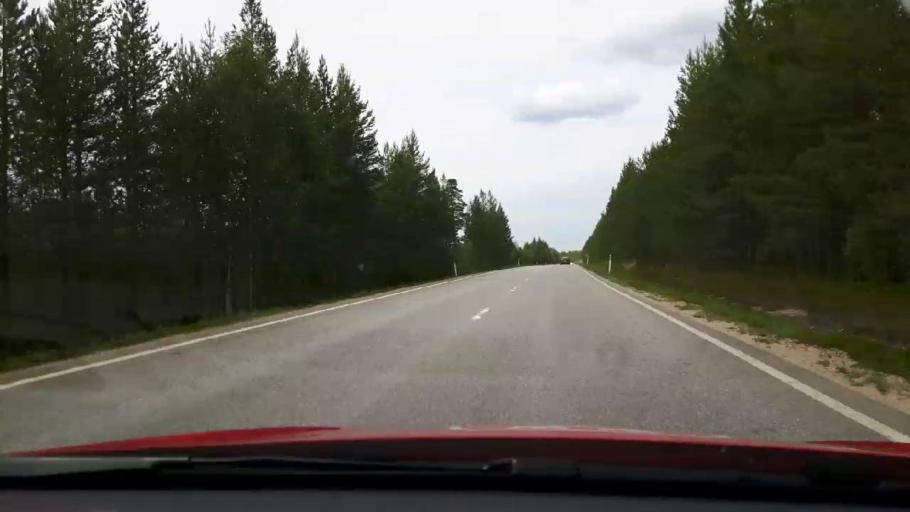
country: SE
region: Jaemtland
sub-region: Harjedalens Kommun
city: Sveg
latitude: 62.0523
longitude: 14.3096
